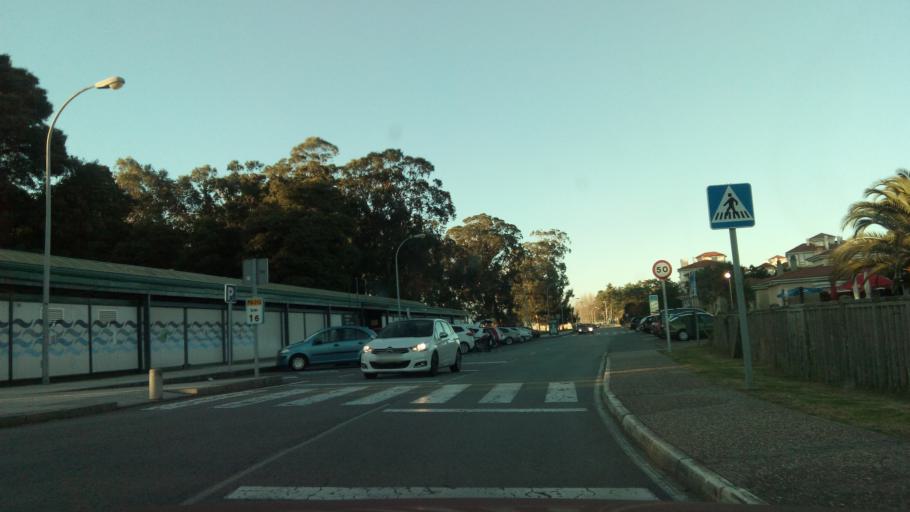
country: ES
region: Galicia
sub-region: Provincia de Pontevedra
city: O Grove
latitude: 42.4837
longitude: -8.8512
